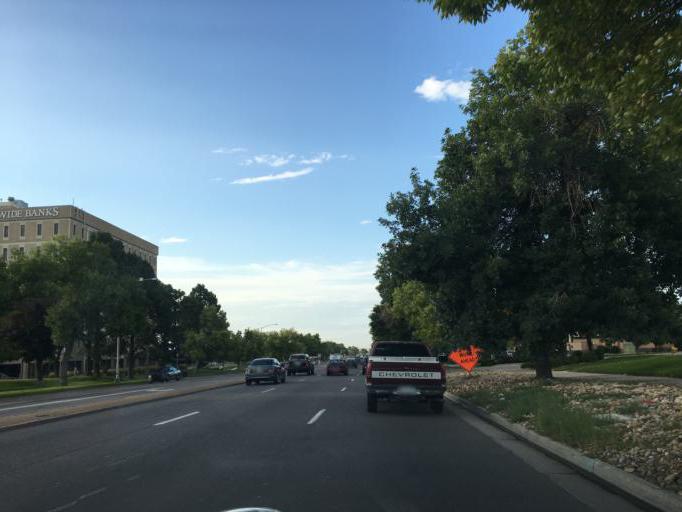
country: US
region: Colorado
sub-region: Adams County
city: Aurora
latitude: 39.7782
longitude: -104.8469
